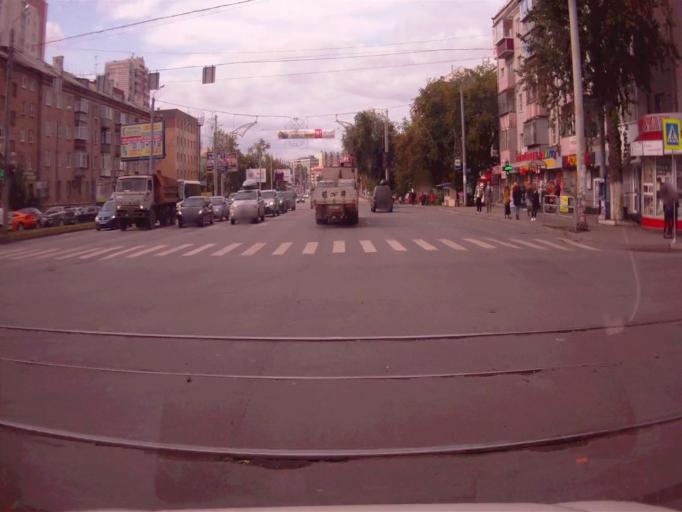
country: RU
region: Chelyabinsk
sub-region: Gorod Chelyabinsk
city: Chelyabinsk
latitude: 55.1448
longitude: 61.3863
